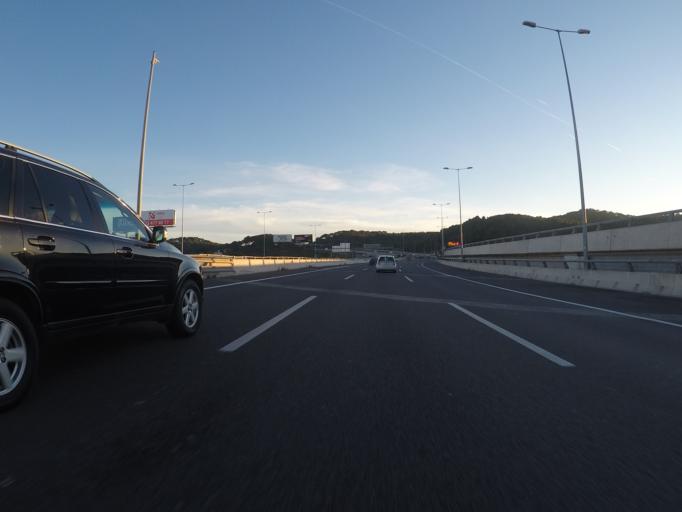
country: ES
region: Catalonia
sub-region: Provincia de Barcelona
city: Ripollet
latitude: 41.4854
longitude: 2.1601
